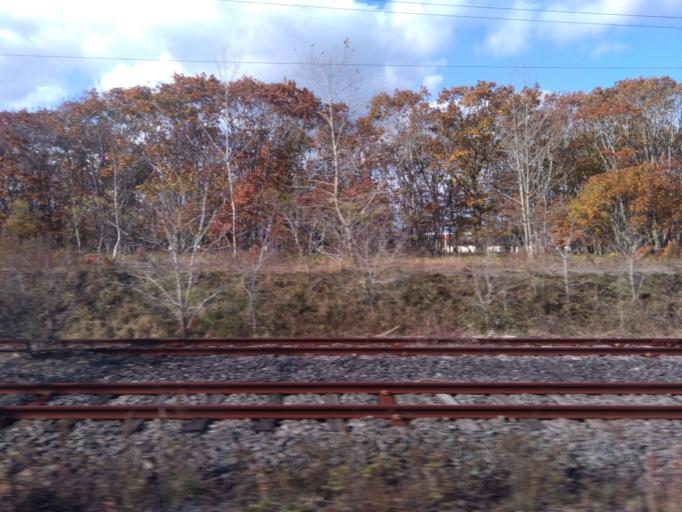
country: JP
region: Hokkaido
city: Shiraoi
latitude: 42.5181
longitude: 141.3005
